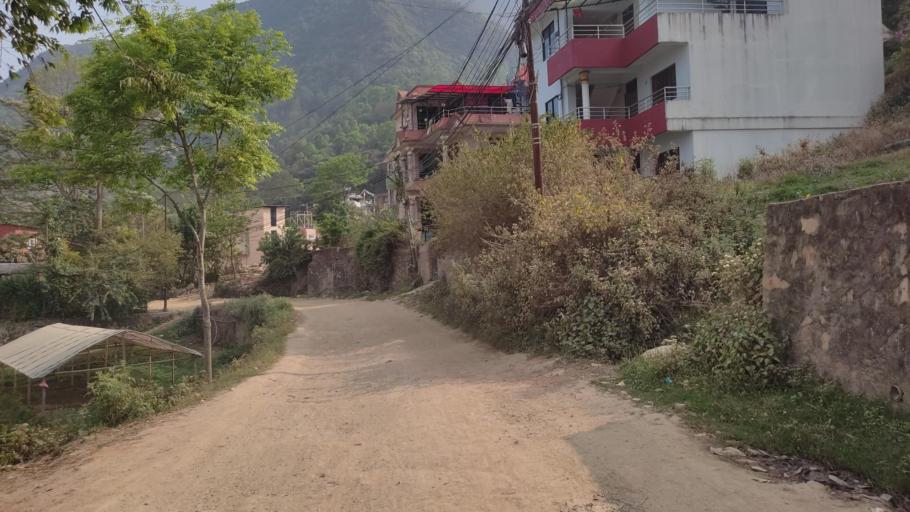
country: NP
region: Central Region
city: Kirtipur
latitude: 27.6640
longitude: 85.2579
